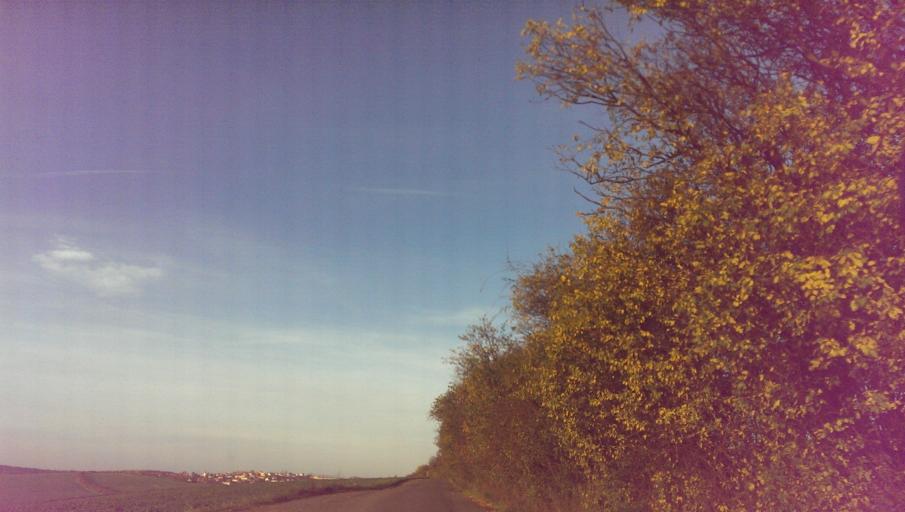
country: CZ
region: Zlin
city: Brezolupy
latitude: 49.1515
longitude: 17.5980
